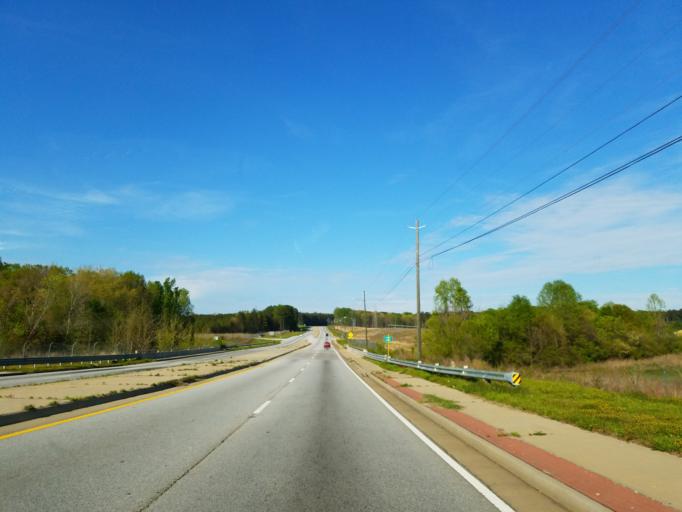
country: US
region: Georgia
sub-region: Cobb County
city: Mableton
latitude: 33.7811
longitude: -84.5092
